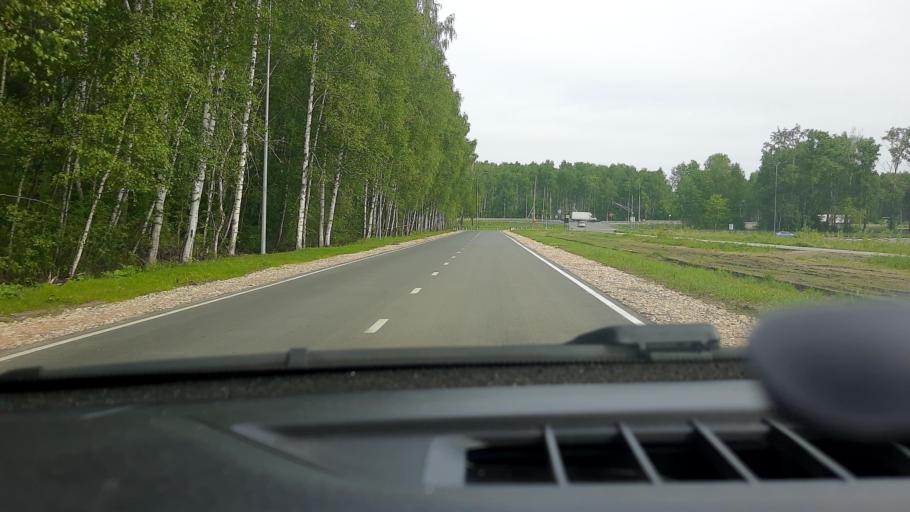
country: RU
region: Nizjnij Novgorod
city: Gorbatovka
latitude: 56.3075
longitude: 43.7693
